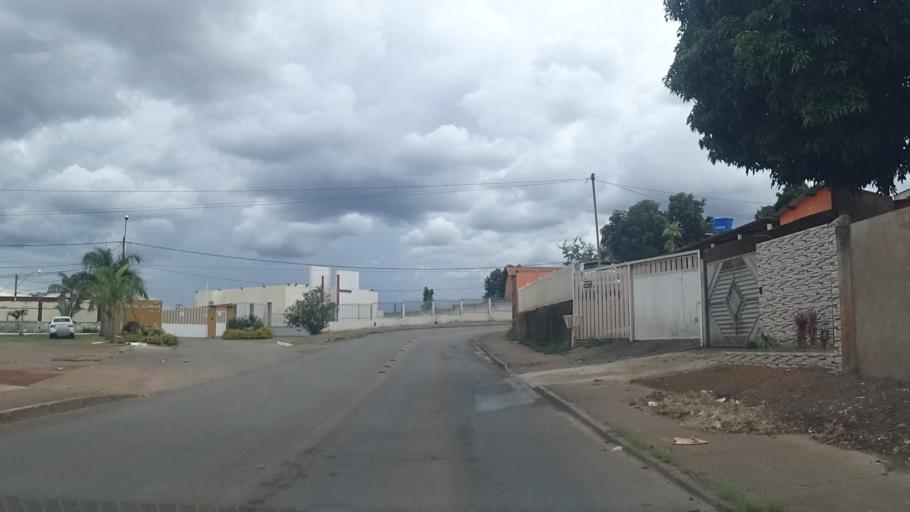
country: BR
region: Federal District
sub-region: Brasilia
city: Brasilia
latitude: -15.8477
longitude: -48.0261
